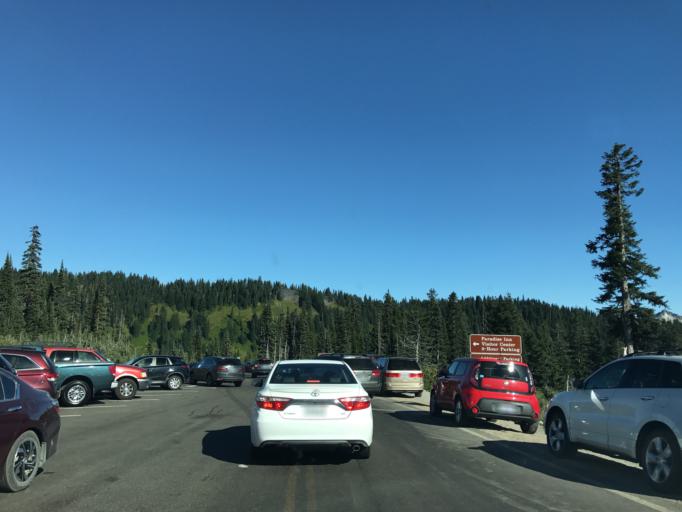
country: US
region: Washington
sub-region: Pierce County
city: Buckley
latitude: 46.7854
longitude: -121.7356
